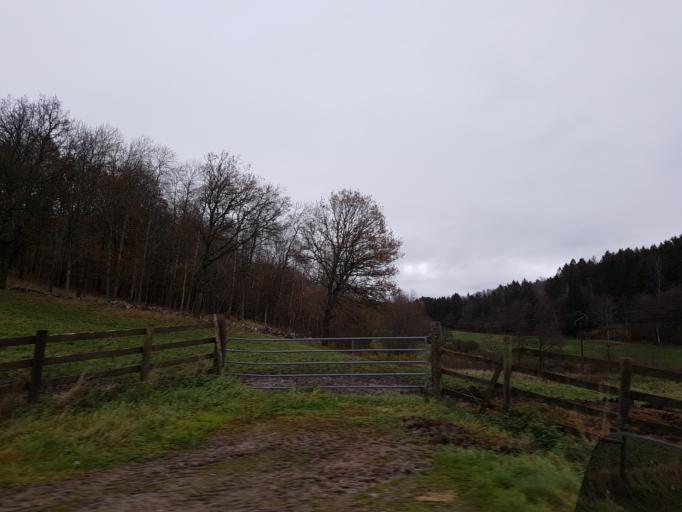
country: SE
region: Vaestra Goetaland
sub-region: Orust
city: Henan
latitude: 58.2477
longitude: 11.7245
